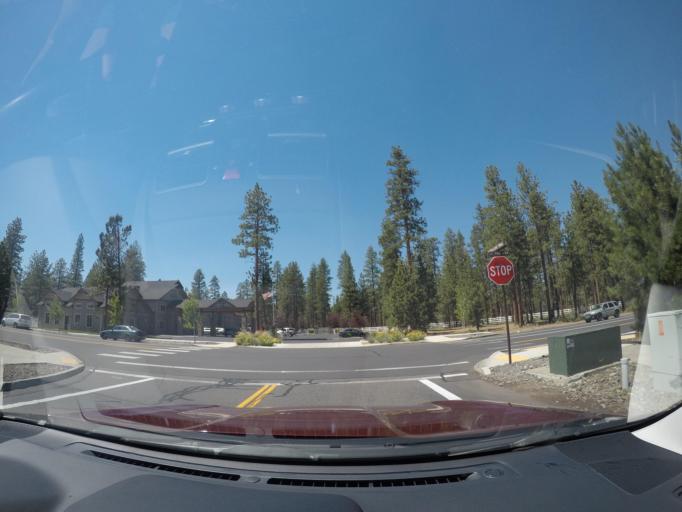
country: US
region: Oregon
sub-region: Deschutes County
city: Sisters
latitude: 44.2979
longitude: -121.5628
